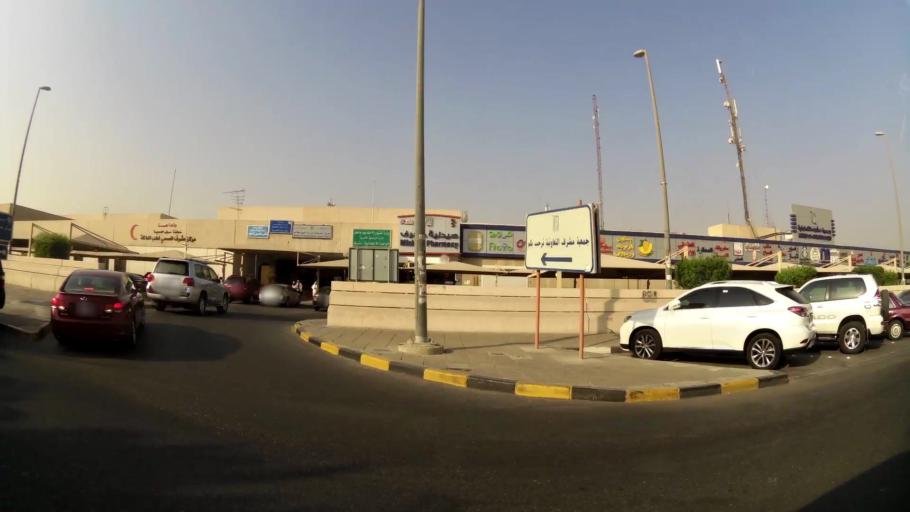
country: KW
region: Muhafazat Hawalli
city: Salwa
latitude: 29.2806
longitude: 48.0702
